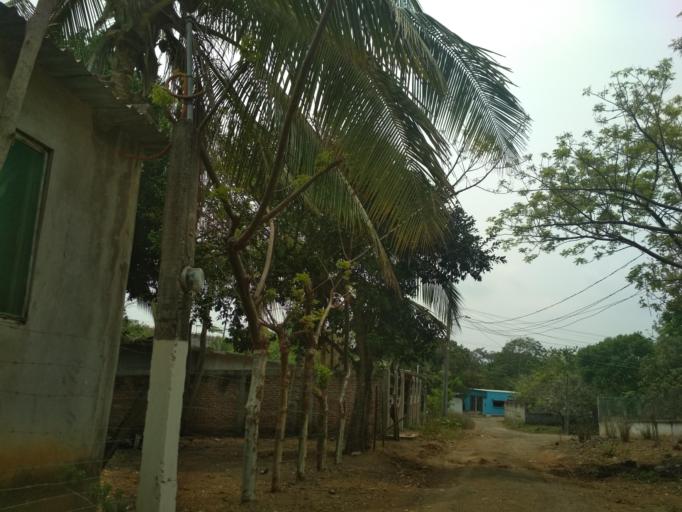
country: MX
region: Veracruz
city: Paso del Toro
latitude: 19.0244
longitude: -96.1378
